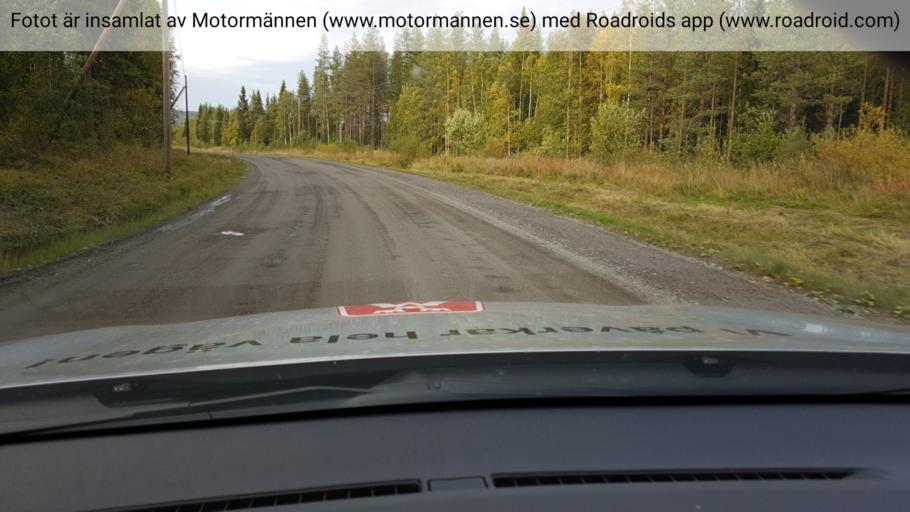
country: SE
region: Jaemtland
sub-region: Stroemsunds Kommun
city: Stroemsund
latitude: 63.9782
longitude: 15.8228
